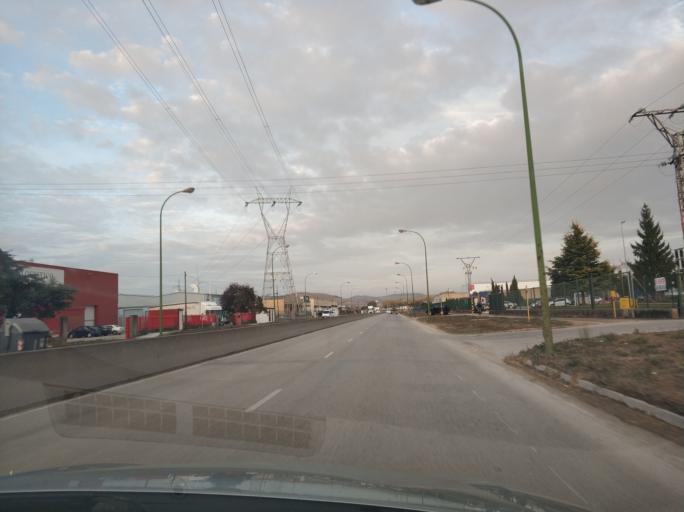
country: ES
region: Castille and Leon
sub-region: Provincia de Burgos
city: Sotragero
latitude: 42.3728
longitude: -3.7275
